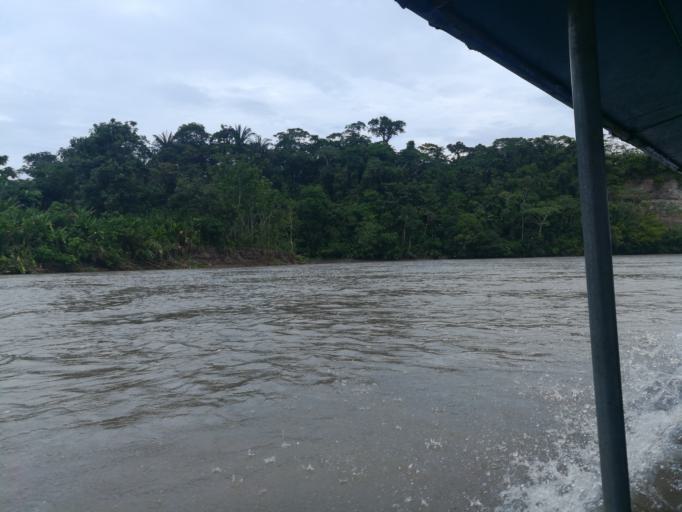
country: EC
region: Orellana
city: Boca Suno
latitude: -0.7633
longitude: -77.1718
